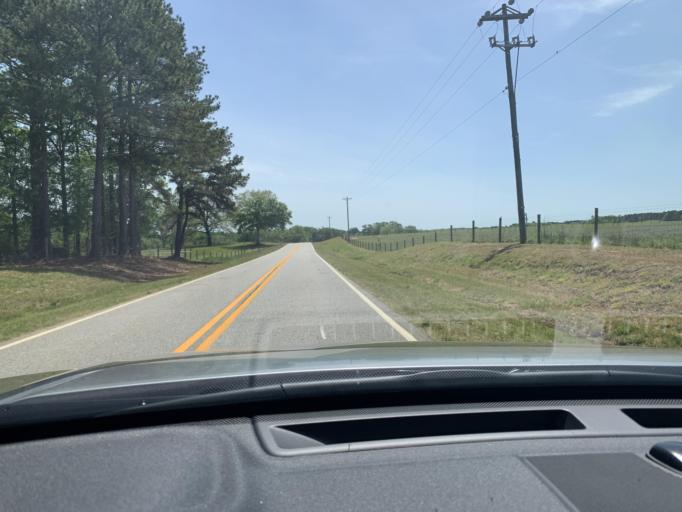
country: US
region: Georgia
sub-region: Oconee County
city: Bogart
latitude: 33.8556
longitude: -83.5476
